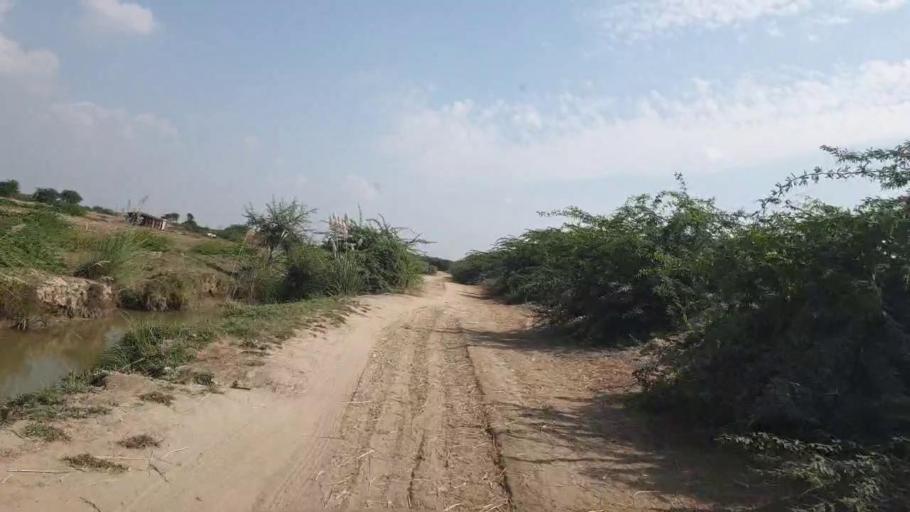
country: PK
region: Sindh
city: Badin
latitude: 24.4774
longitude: 68.6007
